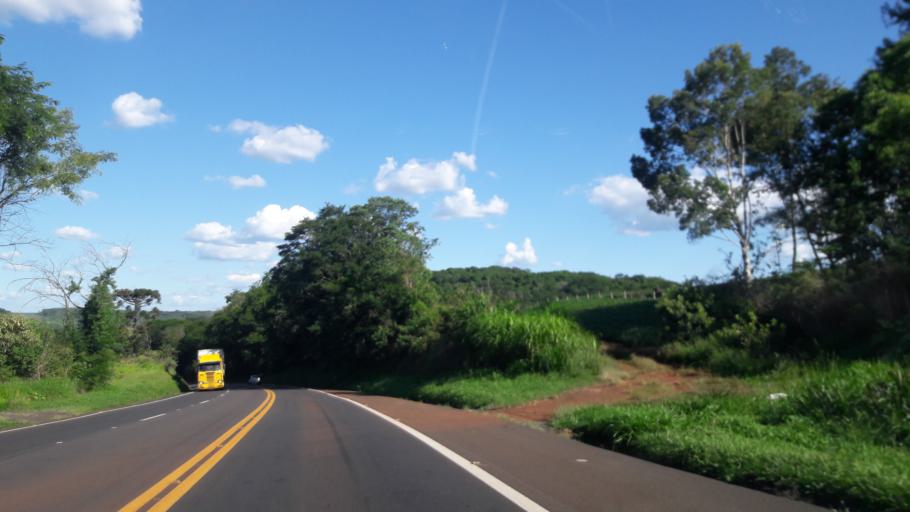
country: BR
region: Parana
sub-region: Laranjeiras Do Sul
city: Laranjeiras do Sul
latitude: -25.4109
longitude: -52.0873
